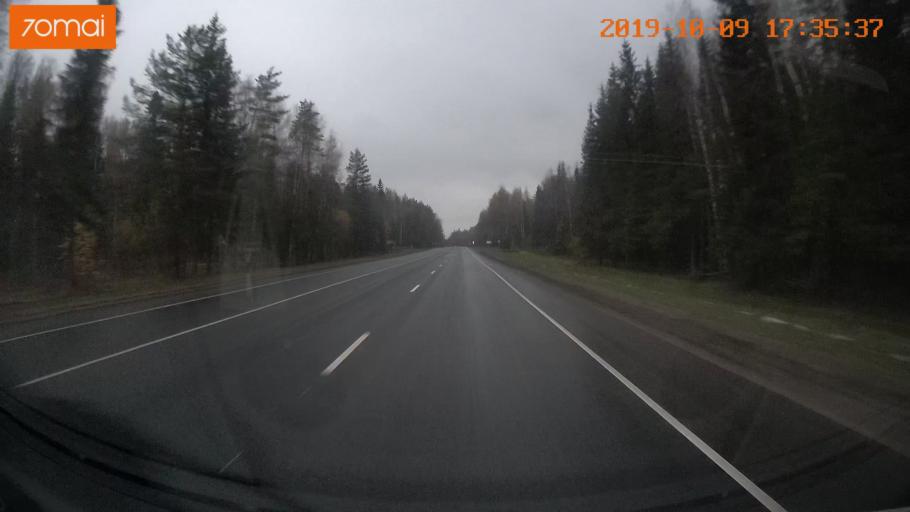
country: RU
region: Ivanovo
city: Bogorodskoye
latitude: 57.0908
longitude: 41.0009
